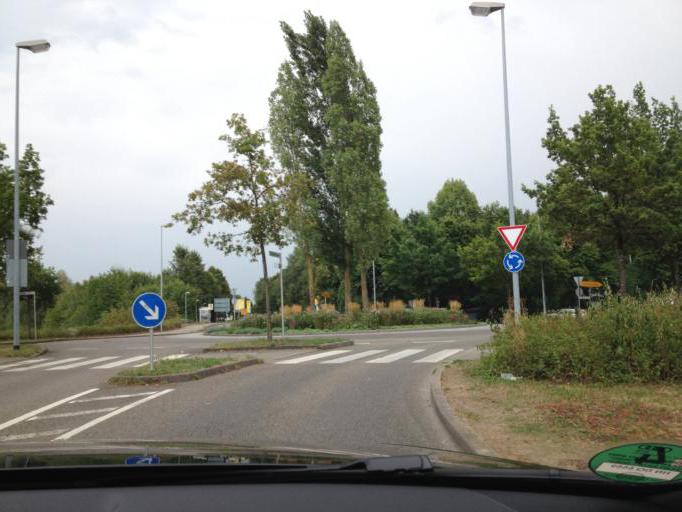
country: DE
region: Baden-Wuerttemberg
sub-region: Regierungsbezirk Stuttgart
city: Leinfelden-Echterdingen
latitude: 48.6917
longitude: 9.1739
